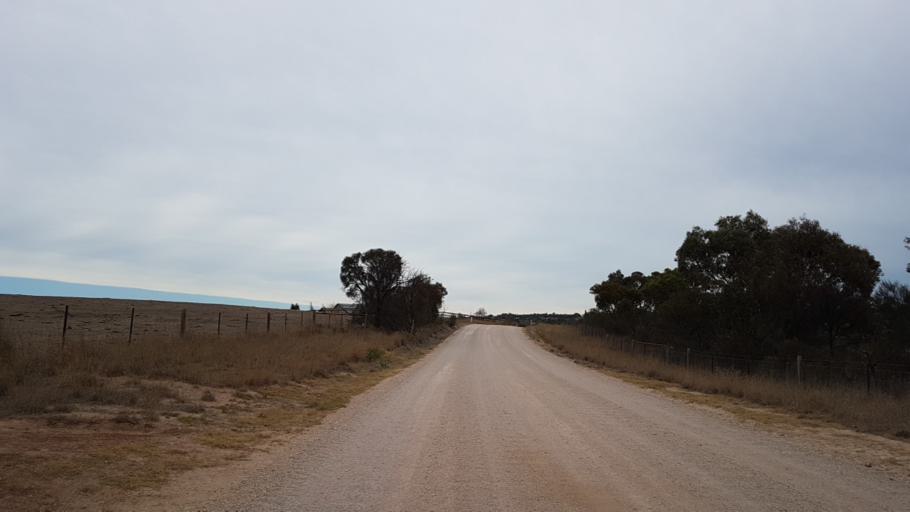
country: AU
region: South Australia
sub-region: Mount Barker
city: Nairne
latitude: -35.0025
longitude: 139.0023
